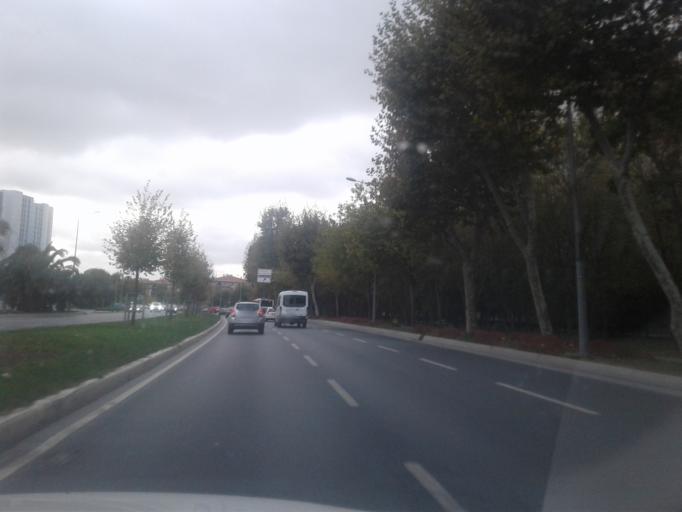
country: TR
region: Istanbul
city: Bahcelievler
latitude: 40.9767
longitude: 28.8559
